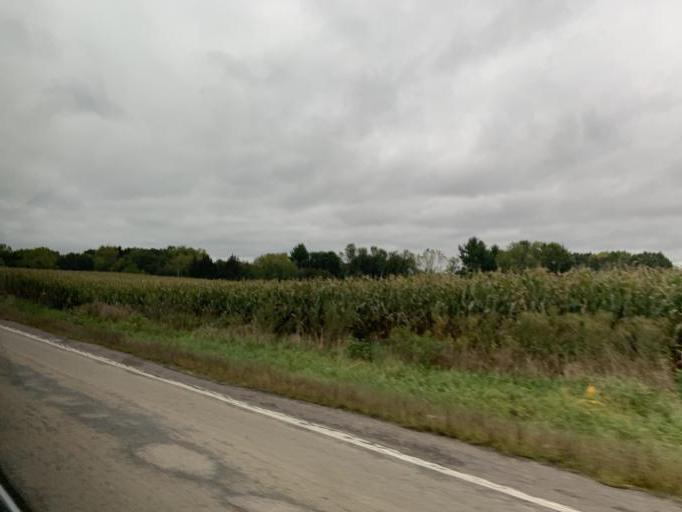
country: US
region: Wisconsin
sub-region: Grant County
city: Muscoda
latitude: 43.2052
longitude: -90.3993
